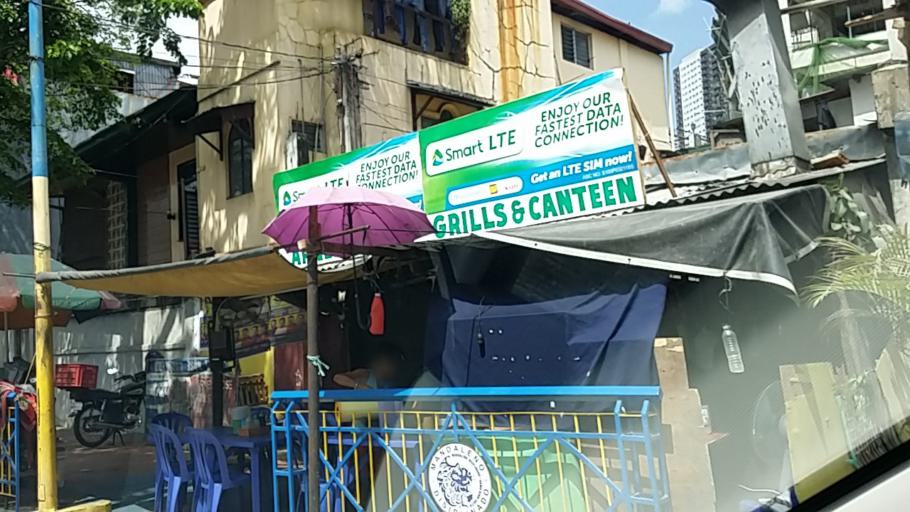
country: PH
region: Metro Manila
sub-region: Mandaluyong
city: Mandaluyong City
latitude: 14.5823
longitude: 121.0467
